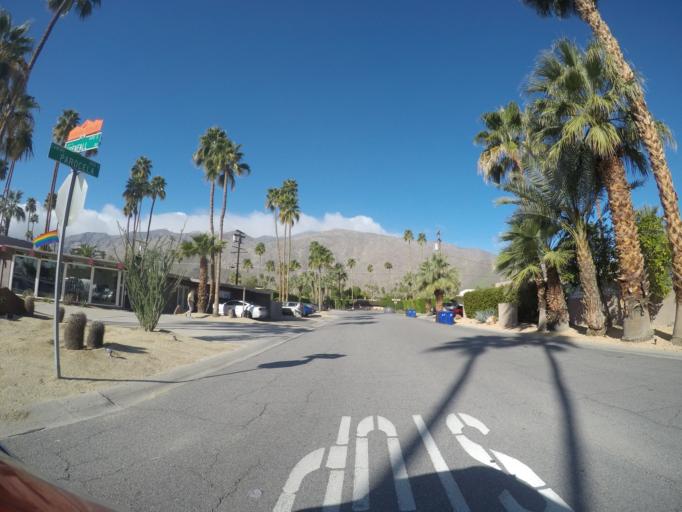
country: US
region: California
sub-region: Riverside County
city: Palm Springs
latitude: 33.8141
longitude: -116.5354
